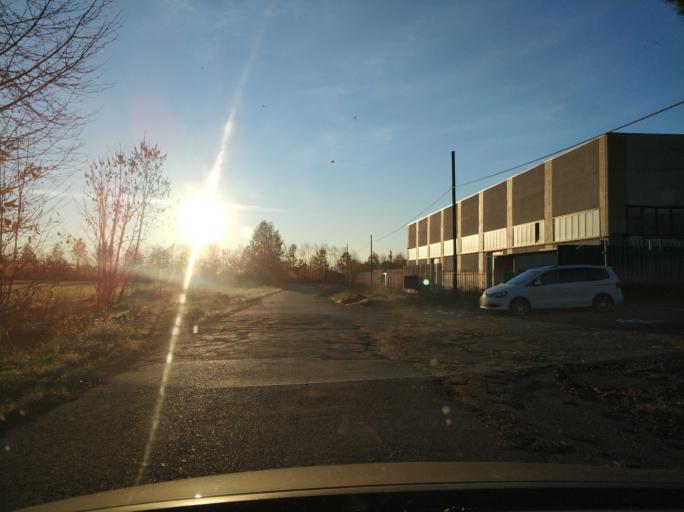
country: IT
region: Piedmont
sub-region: Provincia di Torino
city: Robassomero
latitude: 45.1751
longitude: 7.5951
